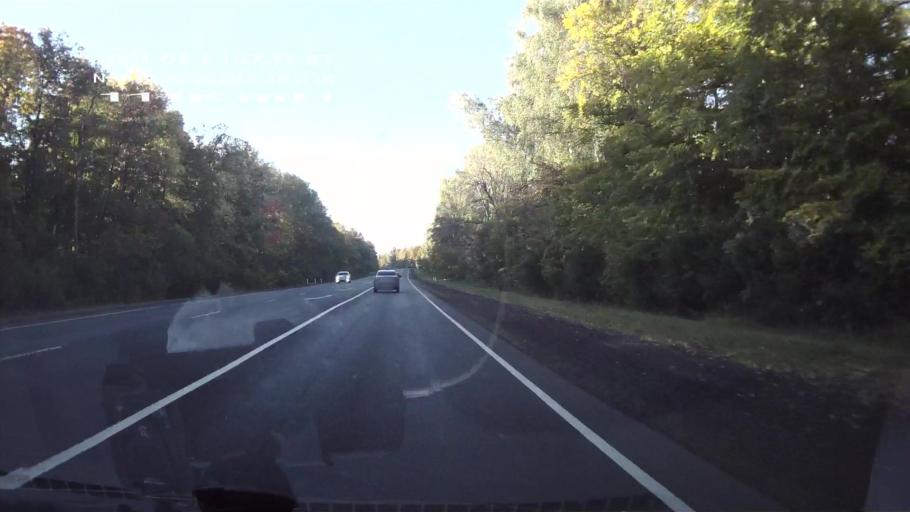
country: RU
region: Chuvashia
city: Tsivil'sk
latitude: 55.8260
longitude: 47.4509
